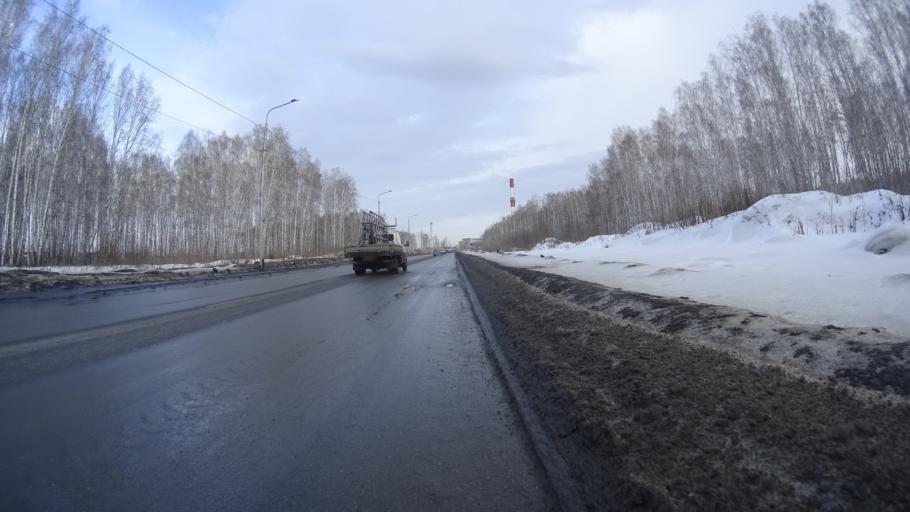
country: RU
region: Chelyabinsk
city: Roshchino
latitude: 55.2085
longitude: 61.3087
